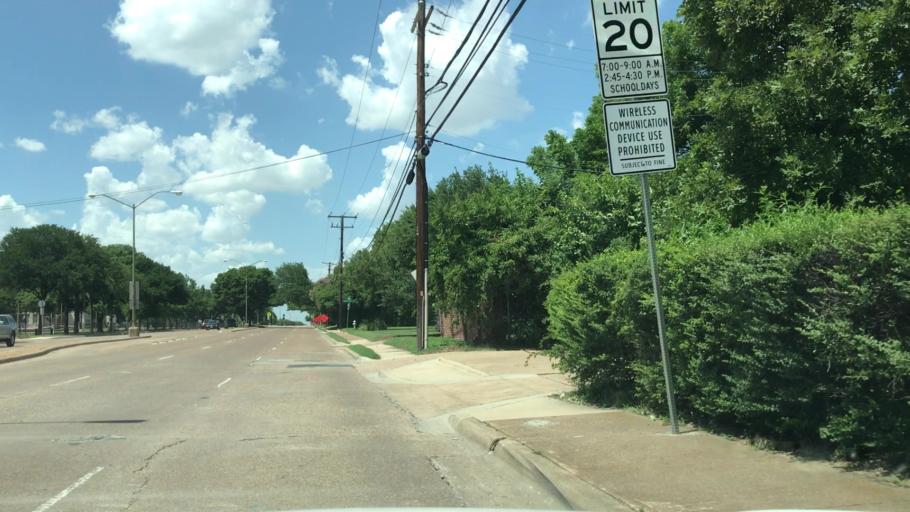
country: US
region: Texas
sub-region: Dallas County
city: University Park
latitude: 32.8806
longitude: -96.8384
